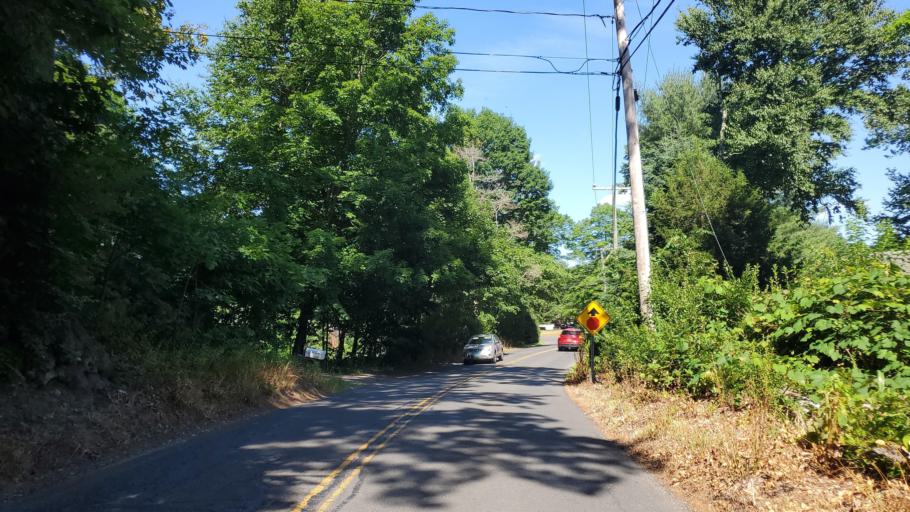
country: US
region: Connecticut
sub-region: Fairfield County
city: Newtown
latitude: 41.3333
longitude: -73.2933
